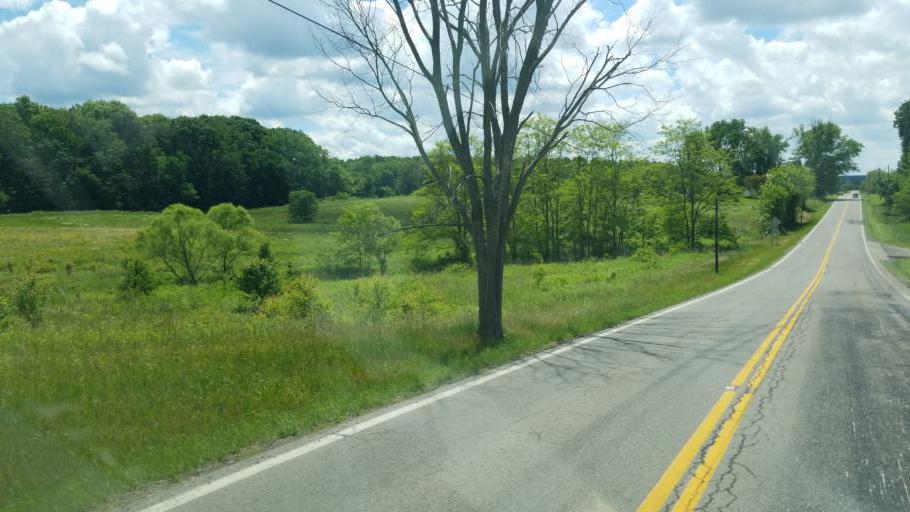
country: US
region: Ohio
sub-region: Richland County
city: Lexington
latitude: 40.6410
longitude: -82.5928
